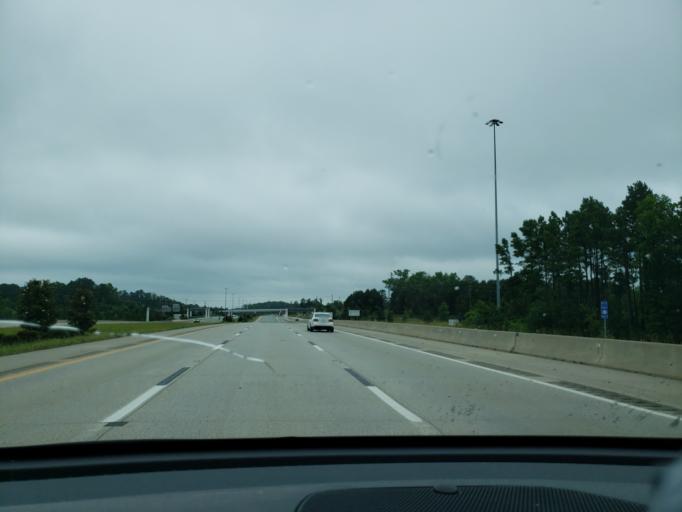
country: US
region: North Carolina
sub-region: Wake County
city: Green Level
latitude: 35.7491
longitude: -78.8917
